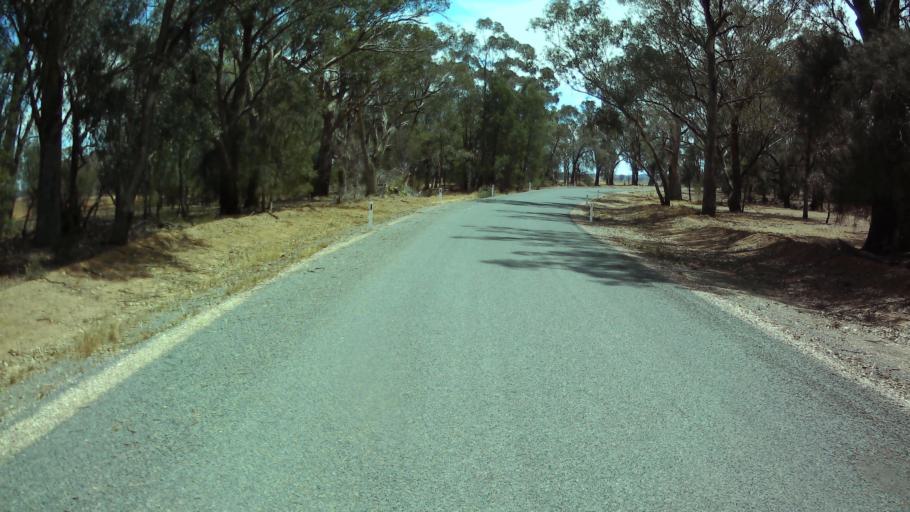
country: AU
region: New South Wales
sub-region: Weddin
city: Grenfell
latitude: -33.6437
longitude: 148.1903
